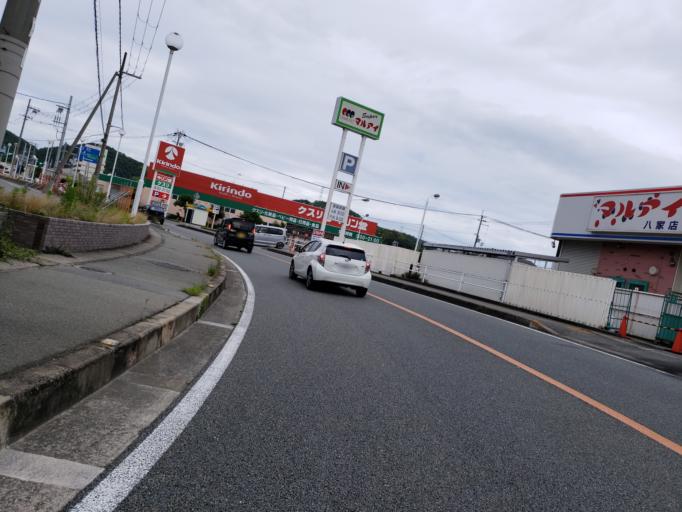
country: JP
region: Hyogo
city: Shirahamacho-usazakiminami
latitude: 34.7839
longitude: 134.7189
